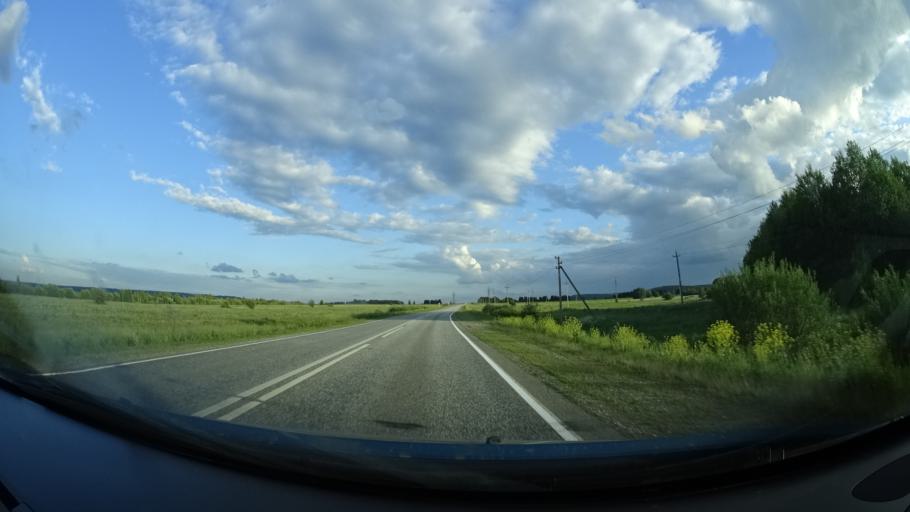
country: RU
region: Perm
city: Barda
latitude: 57.0810
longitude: 55.5427
